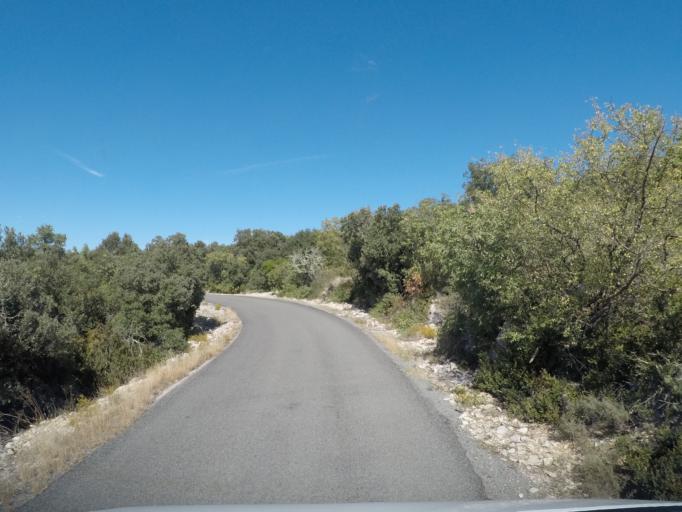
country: FR
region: Languedoc-Roussillon
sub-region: Departement de l'Herault
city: Vailhauques
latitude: 43.7239
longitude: 3.6765
